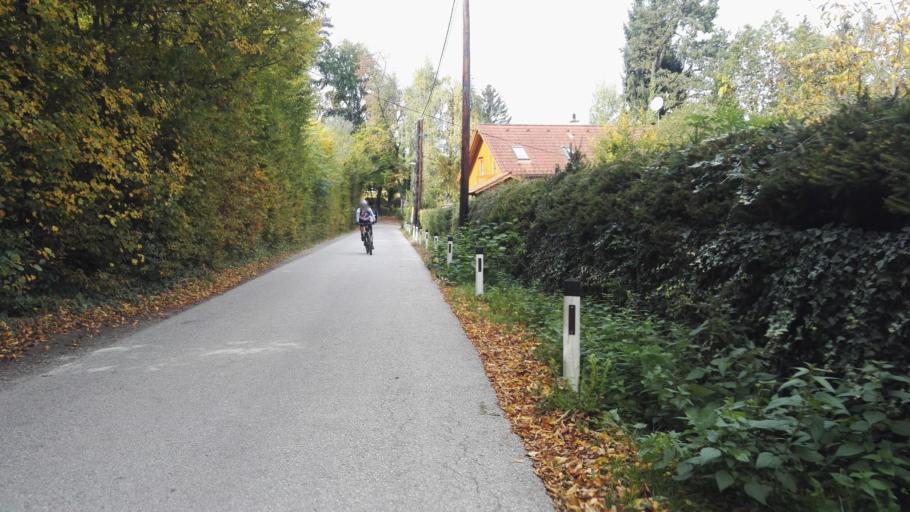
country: AT
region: Styria
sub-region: Graz Stadt
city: Mariatrost
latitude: 47.0944
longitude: 15.4741
